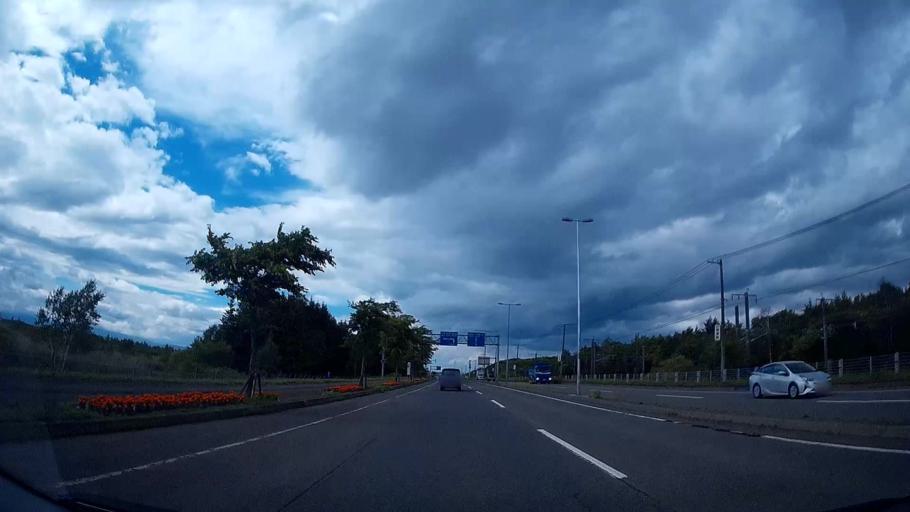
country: JP
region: Hokkaido
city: Chitose
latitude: 42.8140
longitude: 141.6678
